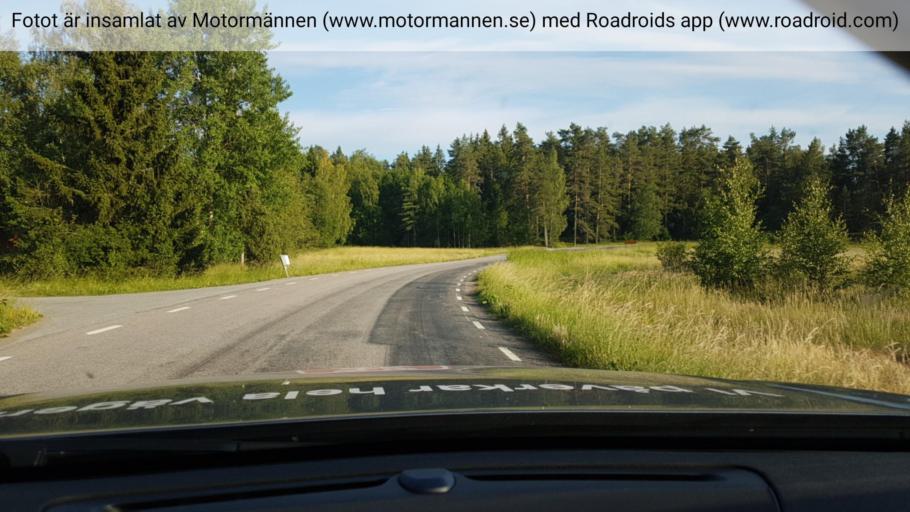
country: SE
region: Uppsala
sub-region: Osthammars Kommun
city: Gimo
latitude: 60.0123
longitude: 18.0660
